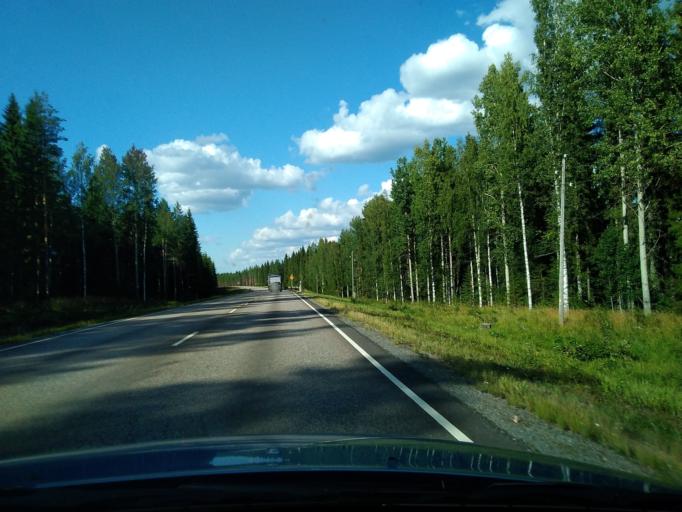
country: FI
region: Pirkanmaa
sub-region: Ylae-Pirkanmaa
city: Maenttae
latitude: 62.0839
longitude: 24.7271
